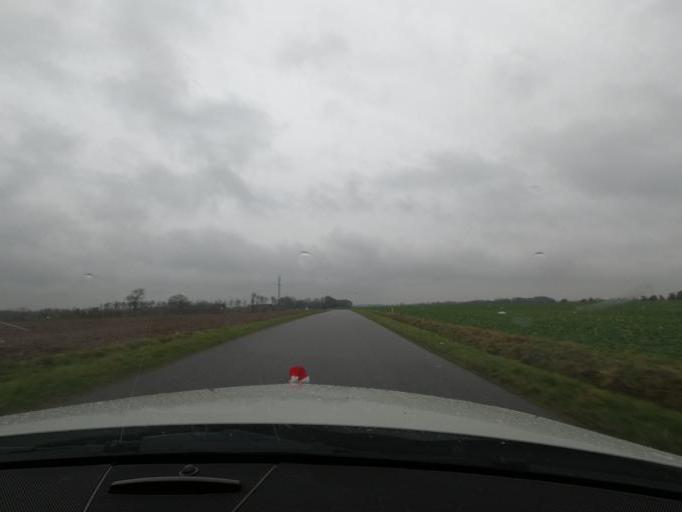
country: DK
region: South Denmark
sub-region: Haderslev Kommune
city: Starup
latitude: 55.2302
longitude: 9.5344
